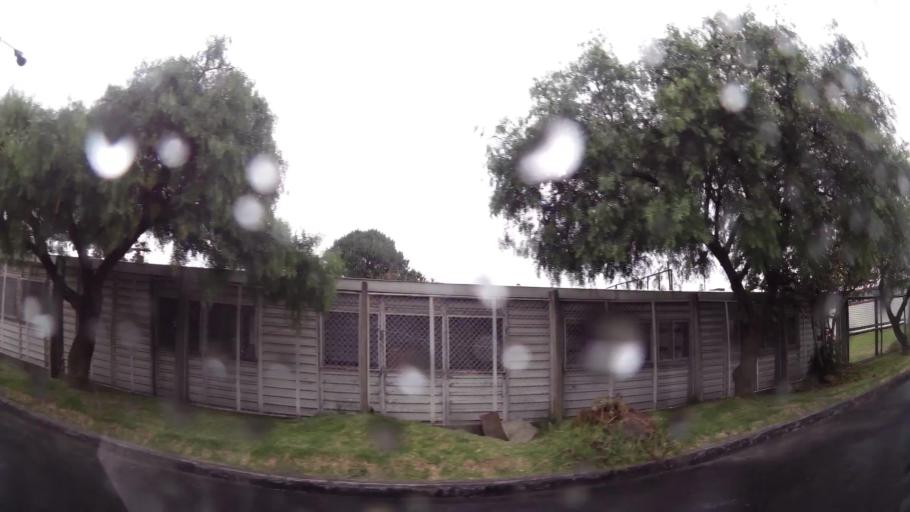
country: CO
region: Bogota D.C.
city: Bogota
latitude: 4.6422
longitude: -74.0922
